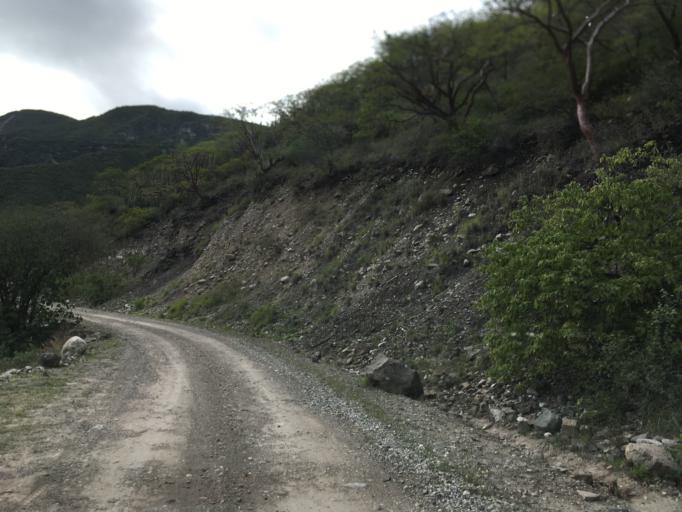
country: MX
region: Hidalgo
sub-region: Metztitlan
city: Fontezuelas
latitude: 20.6422
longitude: -98.9365
